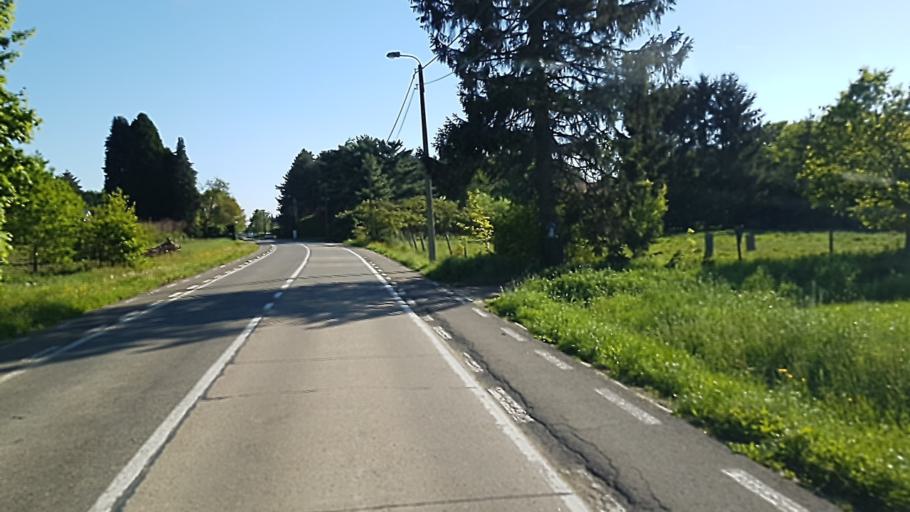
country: BE
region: Flanders
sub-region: Provincie Antwerpen
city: Herenthout
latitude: 51.1141
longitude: 4.7465
